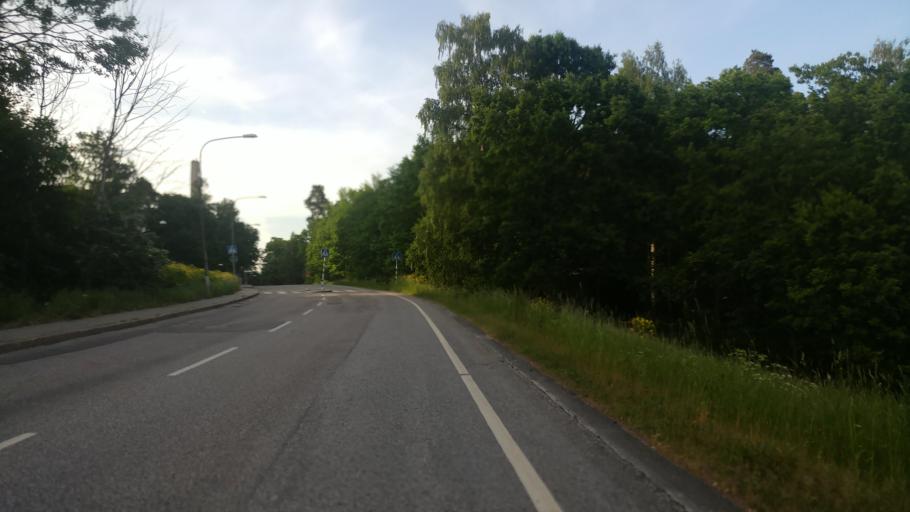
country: SE
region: Stockholm
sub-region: Danderyds Kommun
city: Djursholm
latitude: 59.3695
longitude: 18.0674
